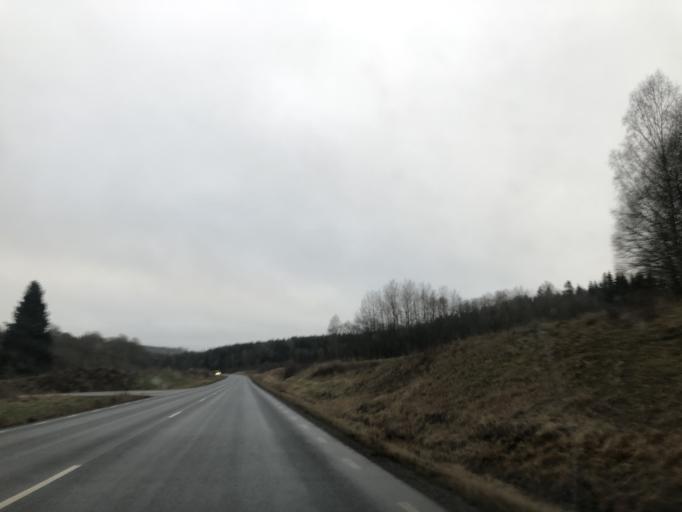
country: SE
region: Vaestra Goetaland
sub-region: Ulricehamns Kommun
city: Ulricehamn
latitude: 57.8262
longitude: 13.2889
